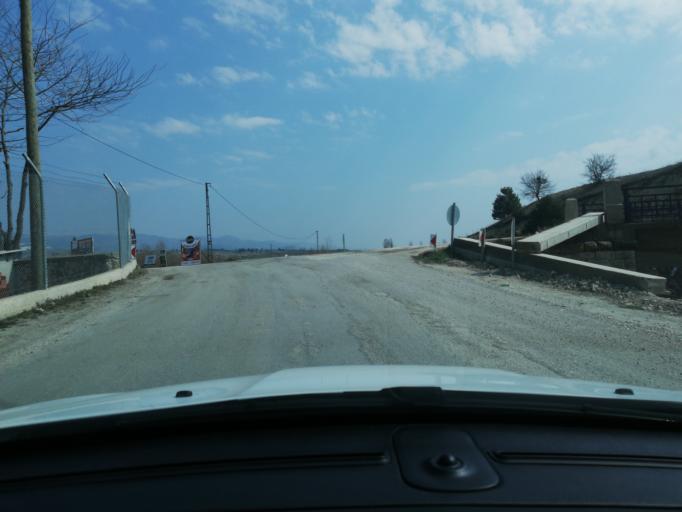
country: TR
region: Kastamonu
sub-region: Cide
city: Kastamonu
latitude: 41.4478
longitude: 33.7651
